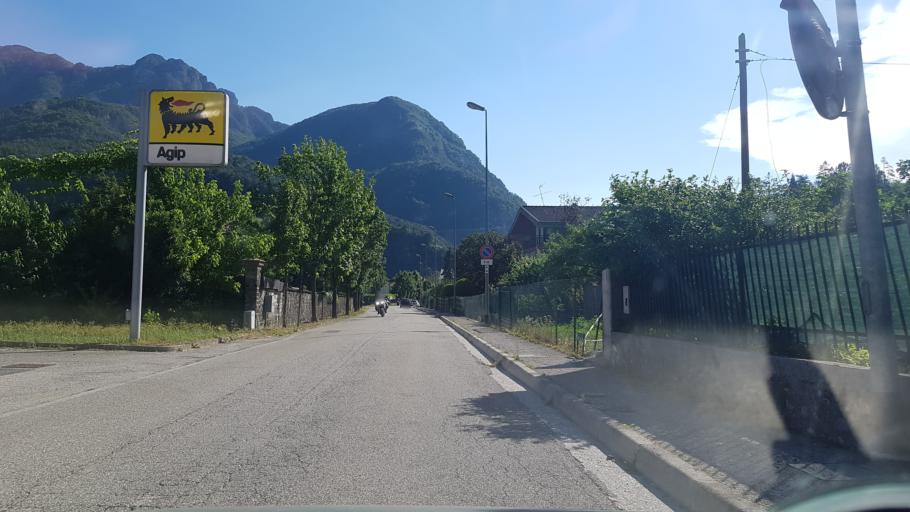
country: IT
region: Friuli Venezia Giulia
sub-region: Provincia di Udine
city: Moggio di Sotto
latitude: 46.4044
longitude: 13.1944
